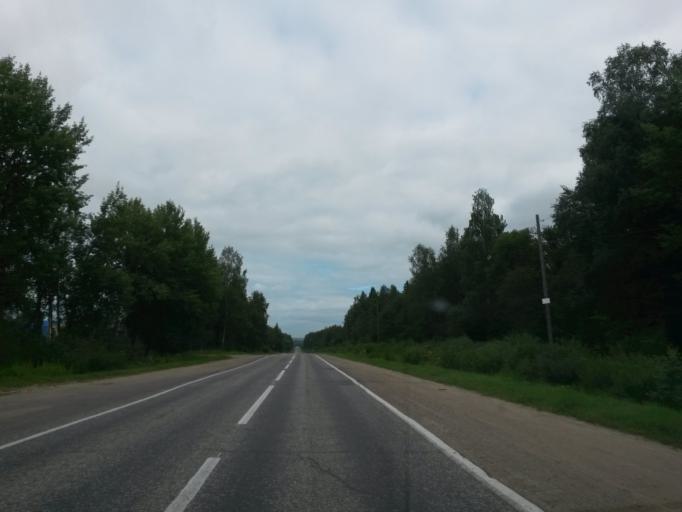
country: RU
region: Jaroslavl
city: Yaroslavl
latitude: 57.4919
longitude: 39.9011
